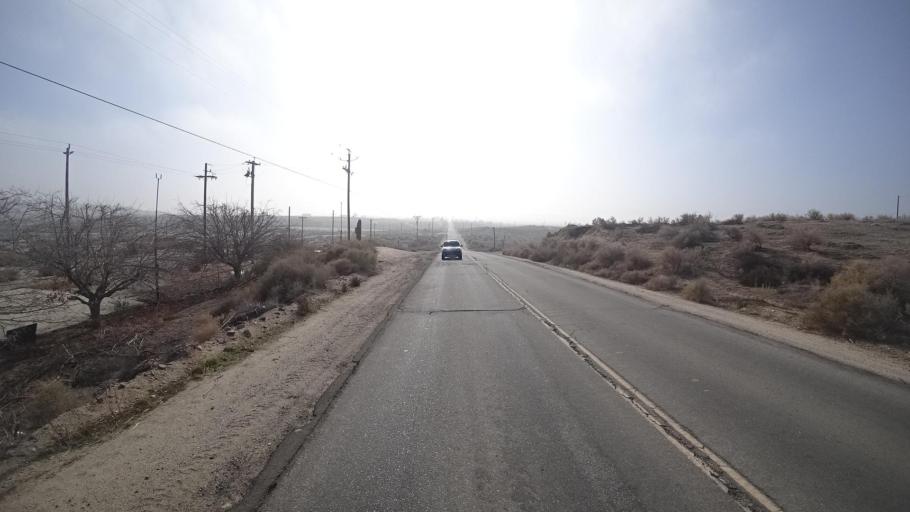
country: US
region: California
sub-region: Kern County
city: Ford City
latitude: 35.1783
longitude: -119.4651
